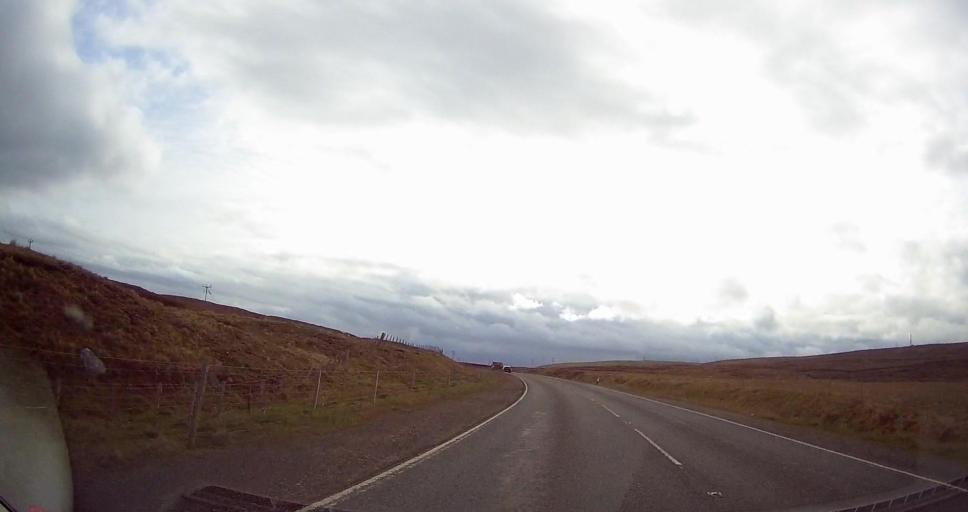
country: GB
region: Scotland
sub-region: Shetland Islands
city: Lerwick
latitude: 60.4410
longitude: -1.2251
